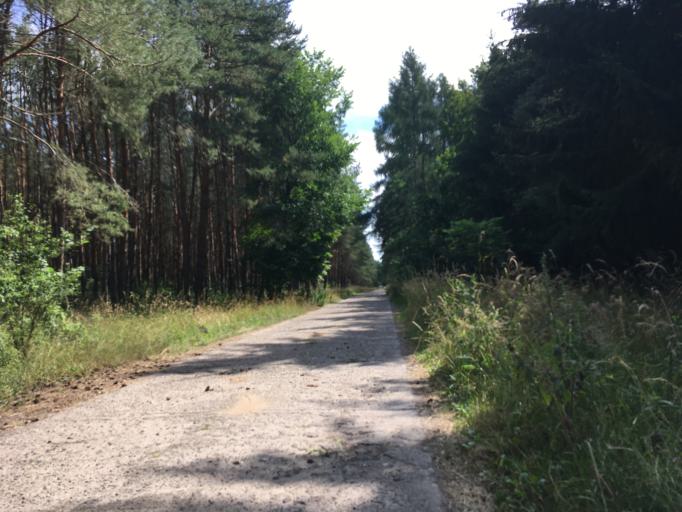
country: DE
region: Brandenburg
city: Passow
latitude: 53.2008
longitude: 14.1164
